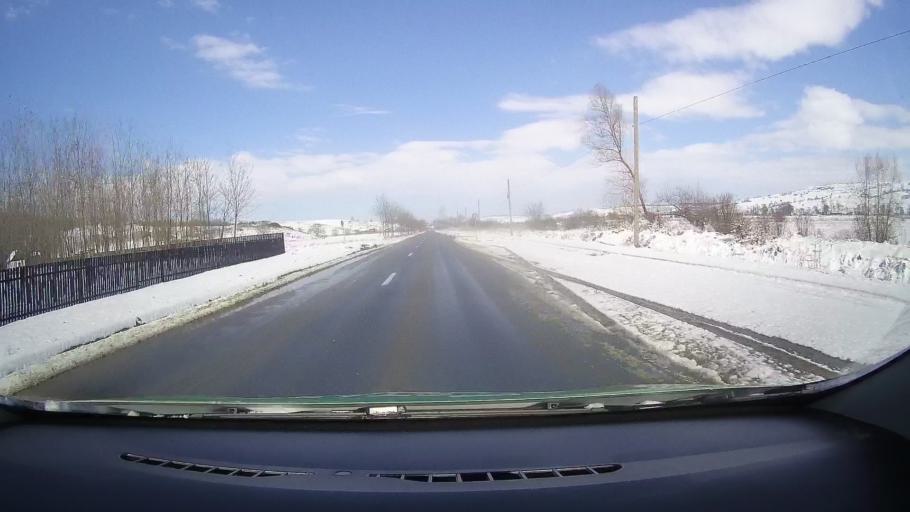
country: RO
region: Sibiu
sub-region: Comuna Nocrich
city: Nocrich
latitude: 45.8726
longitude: 24.4512
